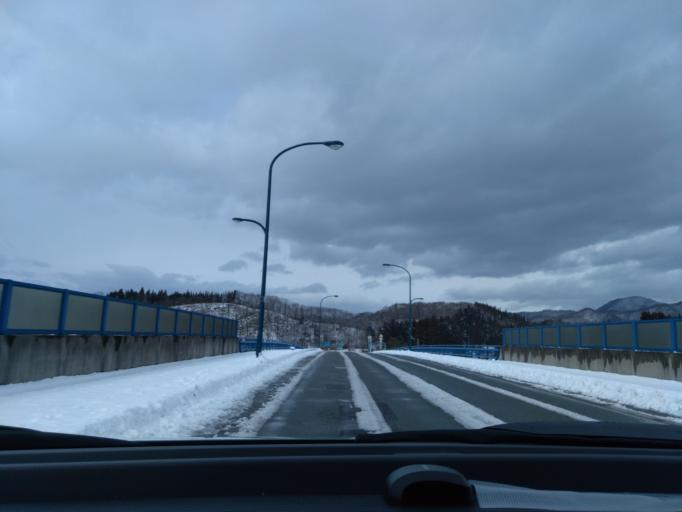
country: JP
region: Akita
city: Kakunodatemachi
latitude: 39.6234
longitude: 140.6298
